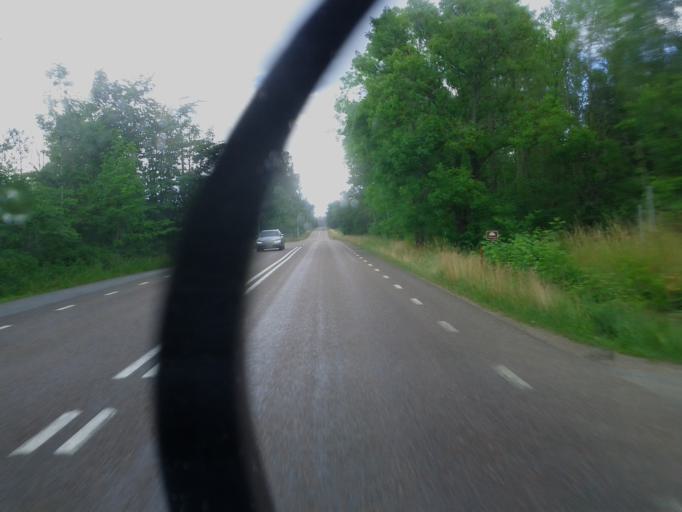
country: SE
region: Vaestmanland
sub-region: Sala Kommun
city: Sala
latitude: 59.8913
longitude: 16.5656
